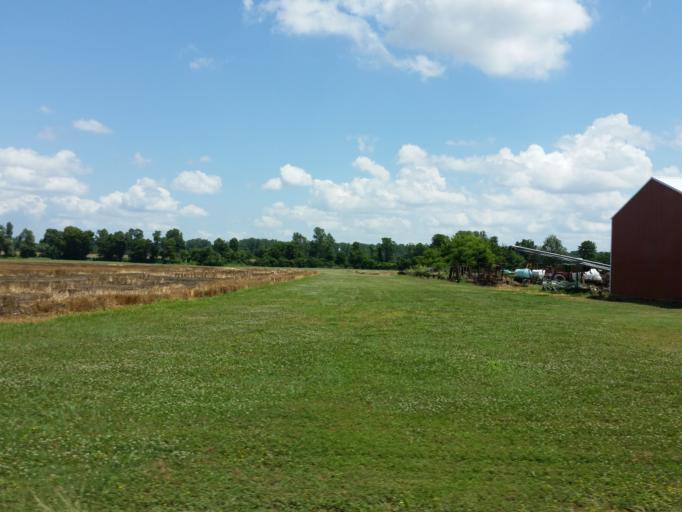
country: US
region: Kentucky
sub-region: Fulton County
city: Hickman
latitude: 36.5563
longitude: -89.2814
